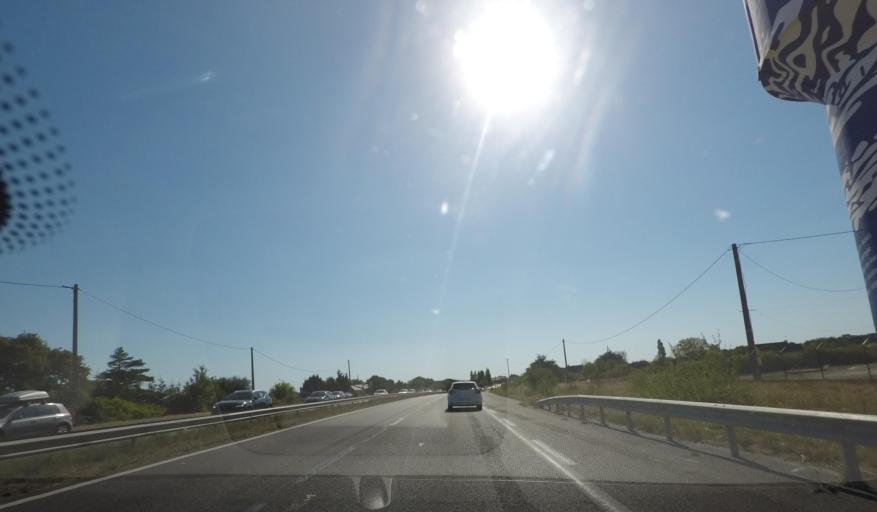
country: FR
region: Pays de la Loire
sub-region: Departement de la Loire-Atlantique
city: Montoir-de-Bretagne
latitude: 47.3303
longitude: -2.1246
